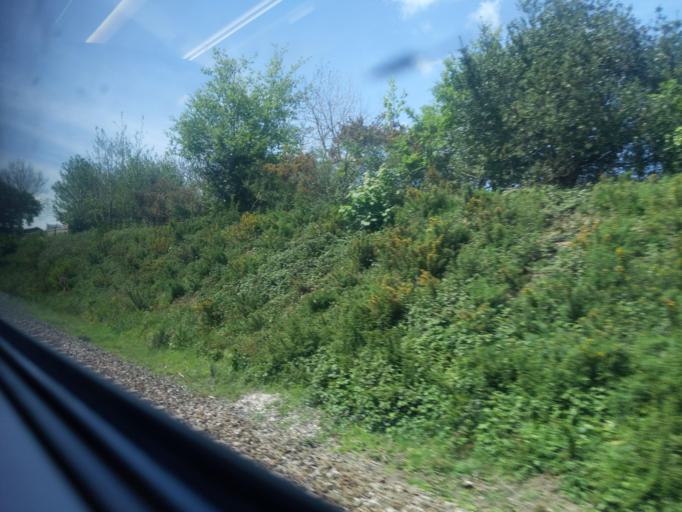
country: GB
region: England
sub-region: Cornwall
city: St Austell
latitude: 50.3389
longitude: -4.7532
